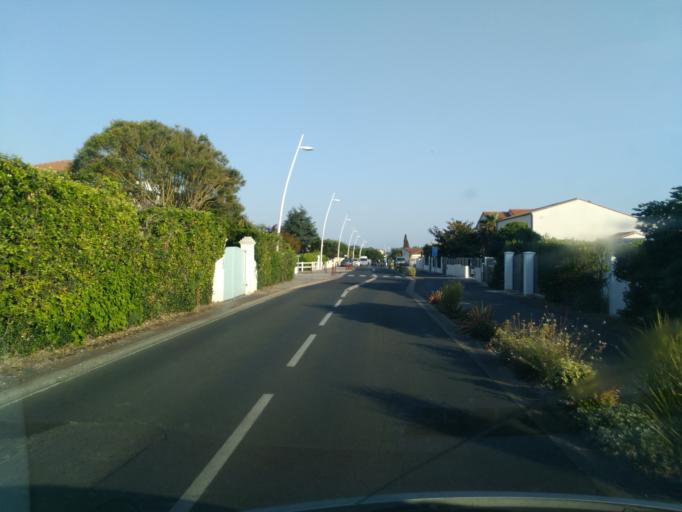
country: FR
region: Poitou-Charentes
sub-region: Departement de la Charente-Maritime
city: Vaux-sur-Mer
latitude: 45.6328
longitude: -1.0581
